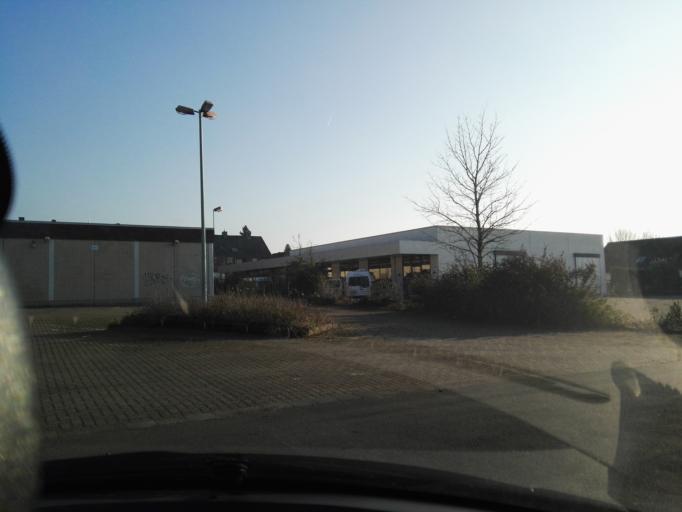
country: DE
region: Lower Saxony
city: Sarstedt
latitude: 52.2454
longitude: 9.8604
